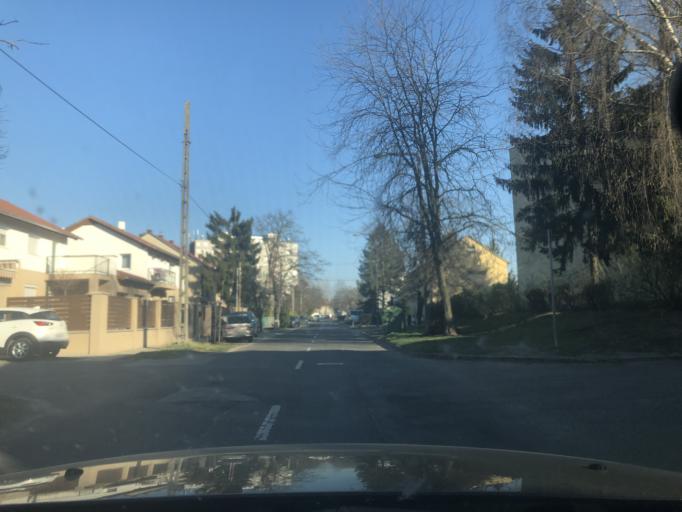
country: HU
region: Pest
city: Dunakeszi
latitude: 47.6462
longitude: 19.1267
